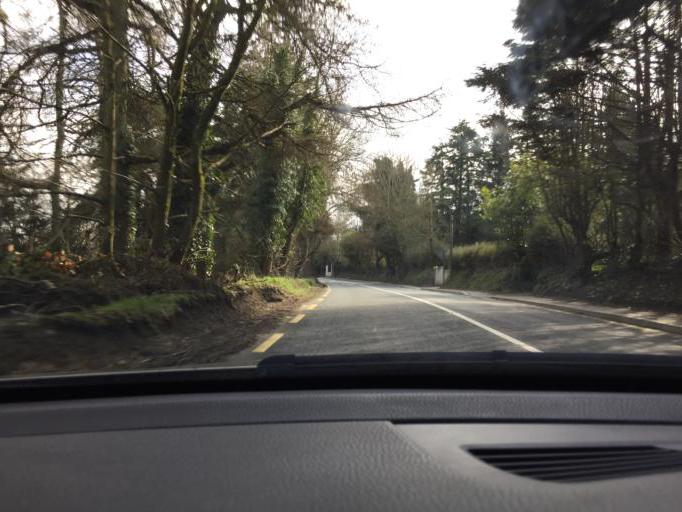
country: IE
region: Leinster
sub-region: South Dublin
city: Saggart
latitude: 53.2475
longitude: -6.4561
